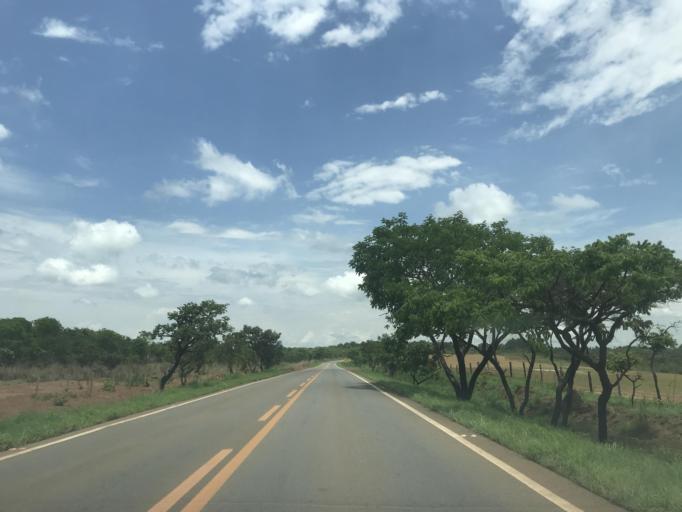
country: BR
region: Goias
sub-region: Luziania
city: Luziania
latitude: -16.3957
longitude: -48.1368
